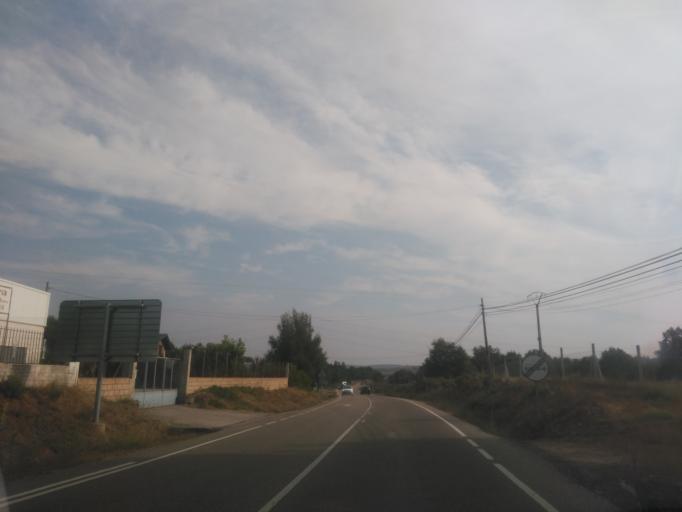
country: ES
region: Castille and Leon
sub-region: Provincia de Zamora
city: Puebla de Sanabria
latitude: 42.0709
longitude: -6.6213
